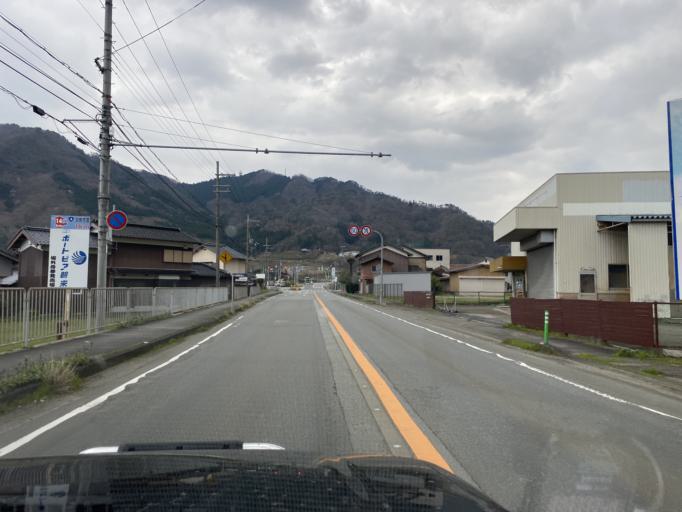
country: JP
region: Hyogo
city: Toyooka
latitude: 35.4223
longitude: 134.7904
